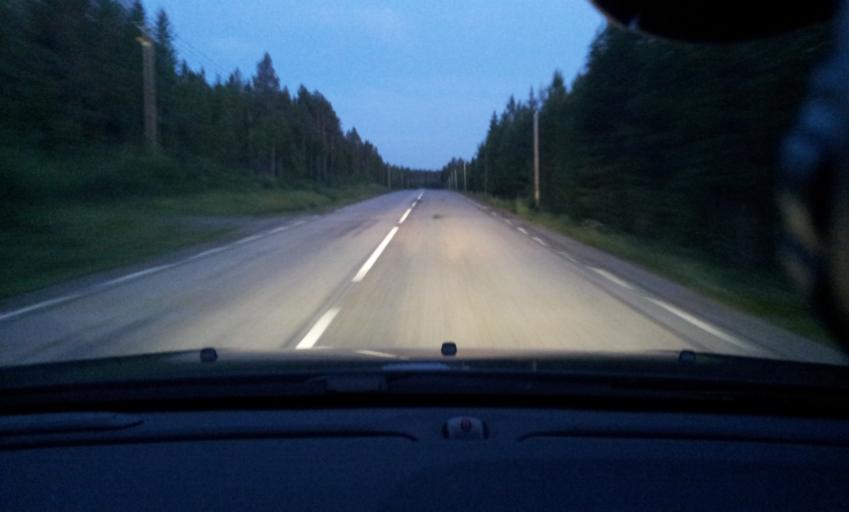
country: SE
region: Jaemtland
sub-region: OEstersunds Kommun
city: Brunflo
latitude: 62.7523
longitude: 14.9842
